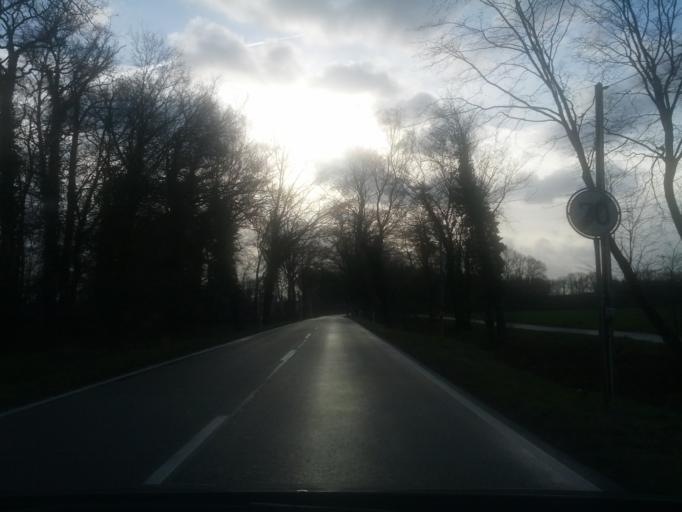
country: DE
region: Lower Saxony
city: Hamersen
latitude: 53.2487
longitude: 9.4830
